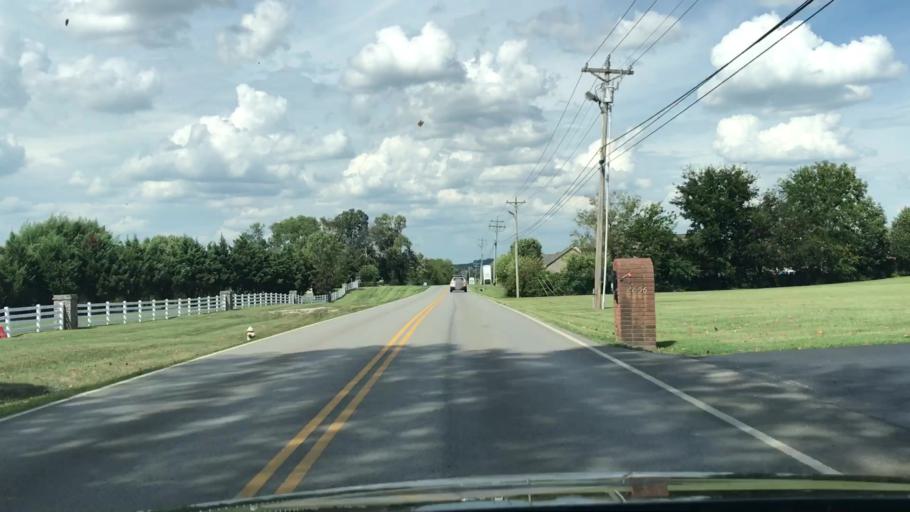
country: US
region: Tennessee
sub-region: Maury County
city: Spring Hill
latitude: 35.7578
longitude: -86.8829
